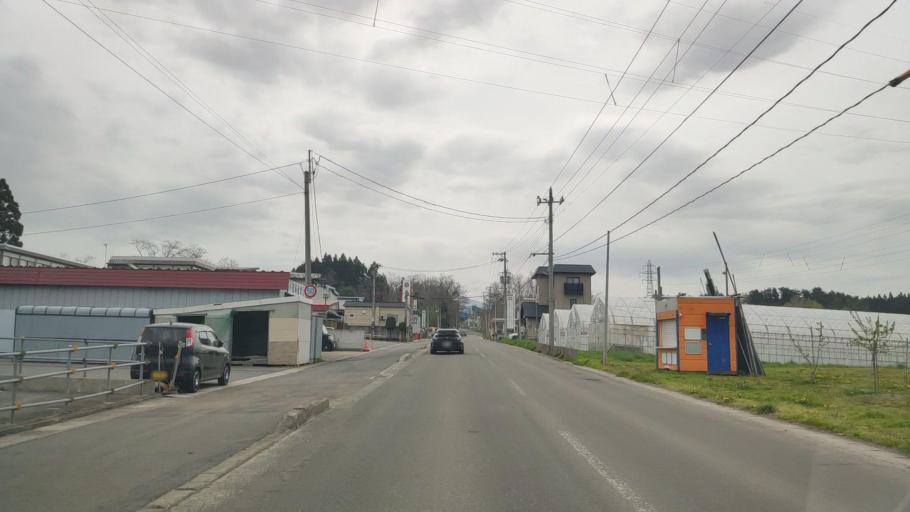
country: JP
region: Aomori
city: Aomori Shi
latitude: 40.7783
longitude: 140.7939
